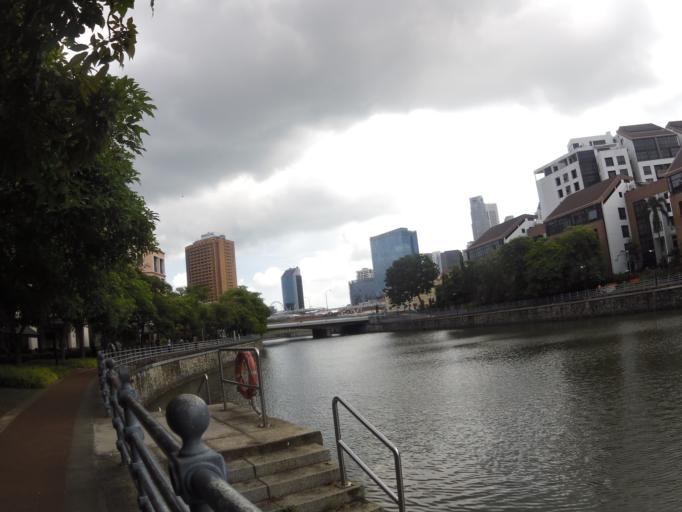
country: SG
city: Singapore
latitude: 1.2909
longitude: 103.8407
